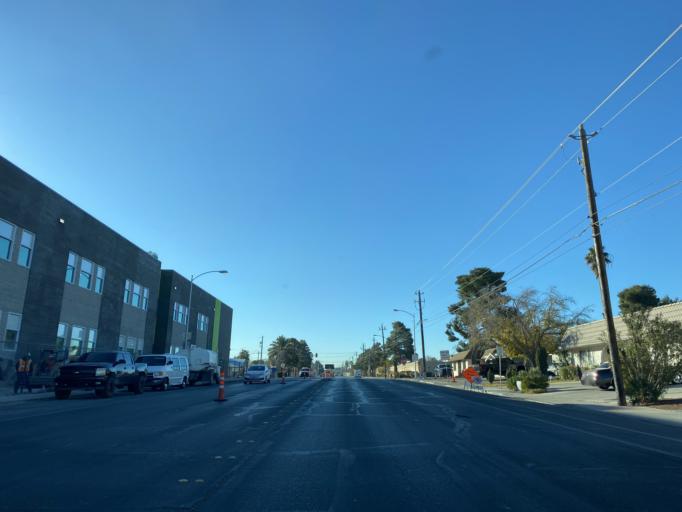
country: US
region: Nevada
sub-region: Clark County
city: Winchester
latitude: 36.1234
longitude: -115.0919
